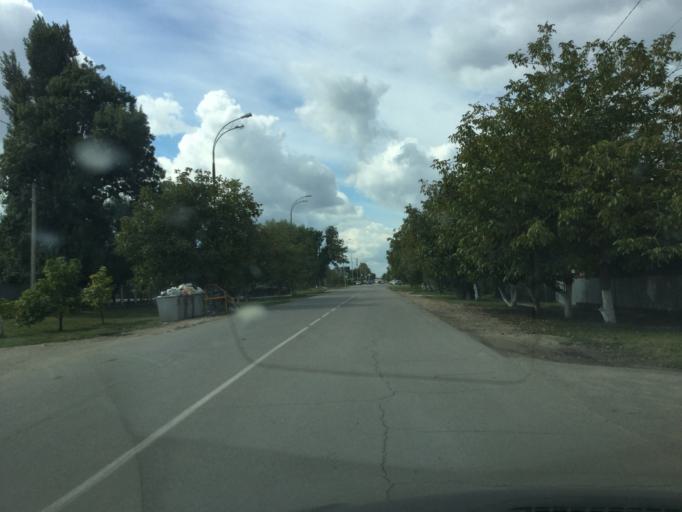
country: RU
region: Krasnodarskiy
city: Slavyansk-na-Kubani
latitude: 45.2528
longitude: 38.1092
